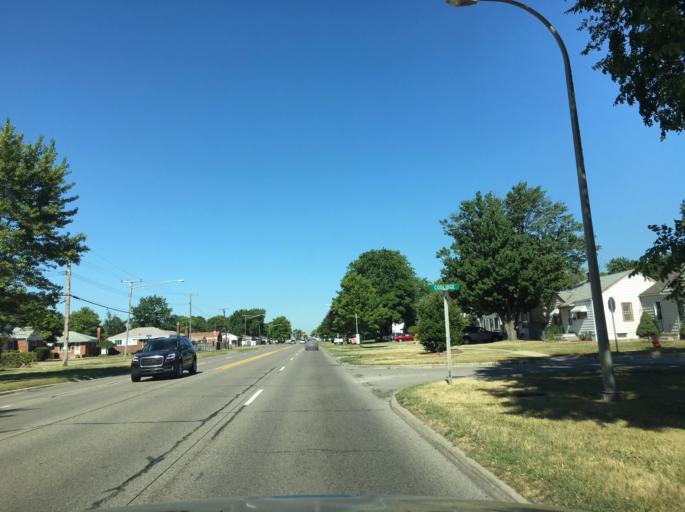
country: US
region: Michigan
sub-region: Macomb County
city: Saint Clair Shores
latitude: 42.5102
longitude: -82.9114
